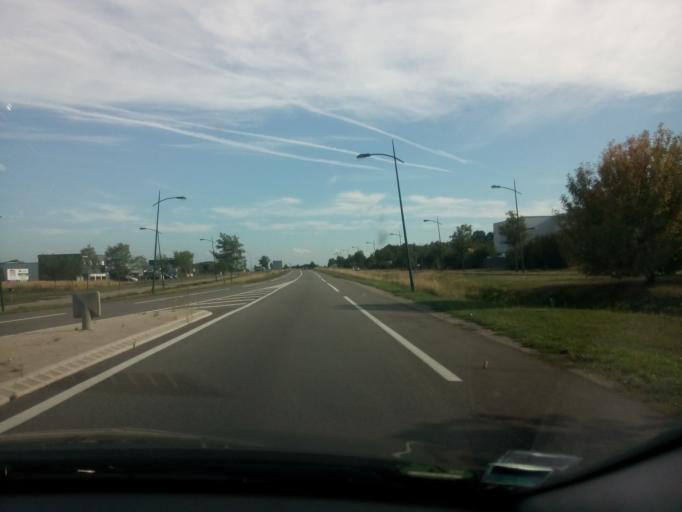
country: FR
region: Alsace
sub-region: Departement du Bas-Rhin
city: Wissembourg
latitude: 49.0214
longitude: 7.9655
